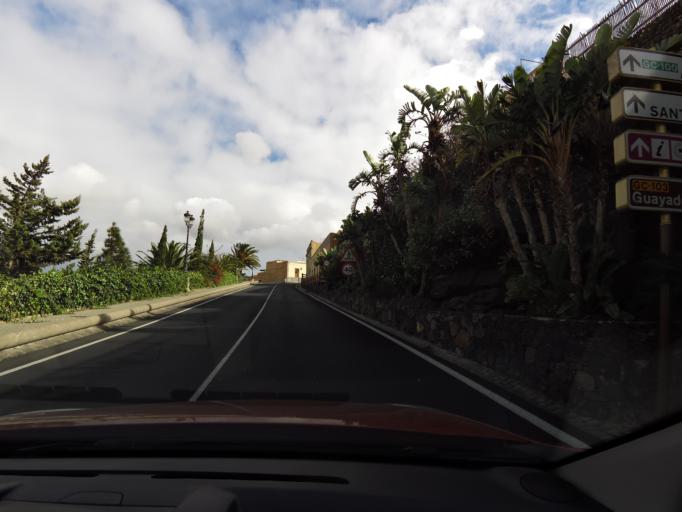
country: ES
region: Canary Islands
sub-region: Provincia de Las Palmas
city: Aguimes
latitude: 27.9075
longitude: -15.4441
